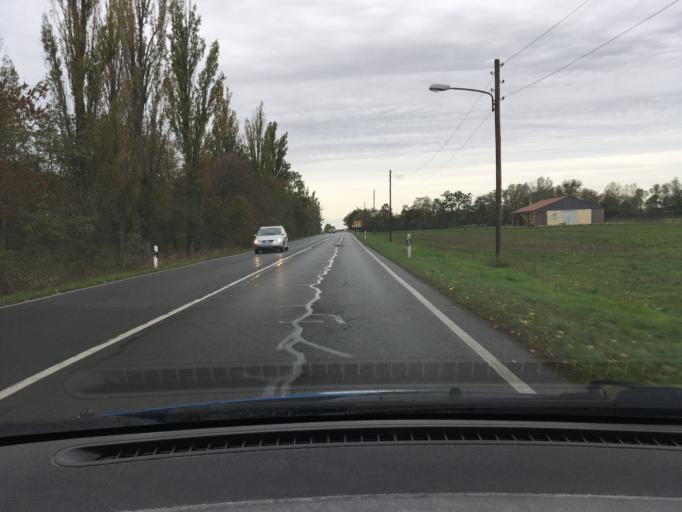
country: DE
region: Saxony-Anhalt
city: Zerbst
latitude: 51.9753
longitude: 12.0650
